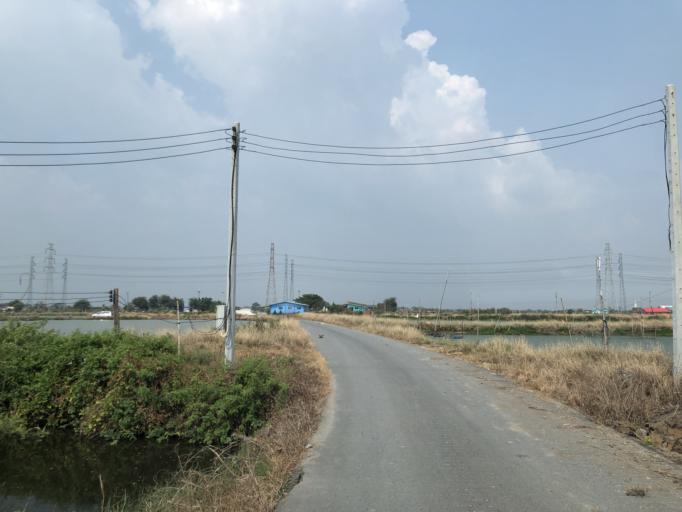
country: TH
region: Samut Prakan
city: Bang Bo
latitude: 13.5422
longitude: 100.8805
